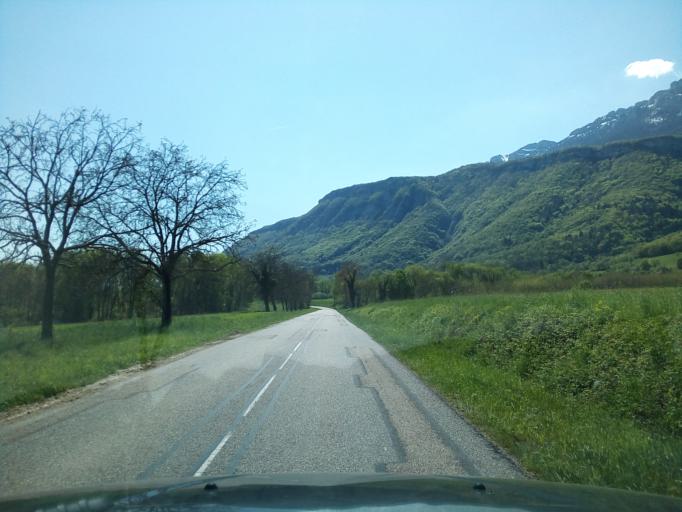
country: FR
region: Rhone-Alpes
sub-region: Departement de l'Isere
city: Barraux
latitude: 45.4457
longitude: 5.9880
